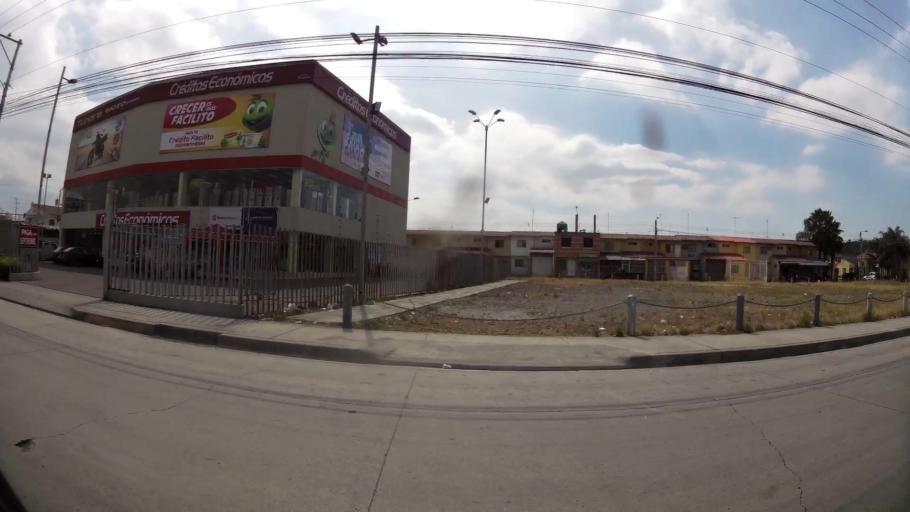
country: EC
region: Guayas
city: Eloy Alfaro
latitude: -2.0835
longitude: -79.9177
